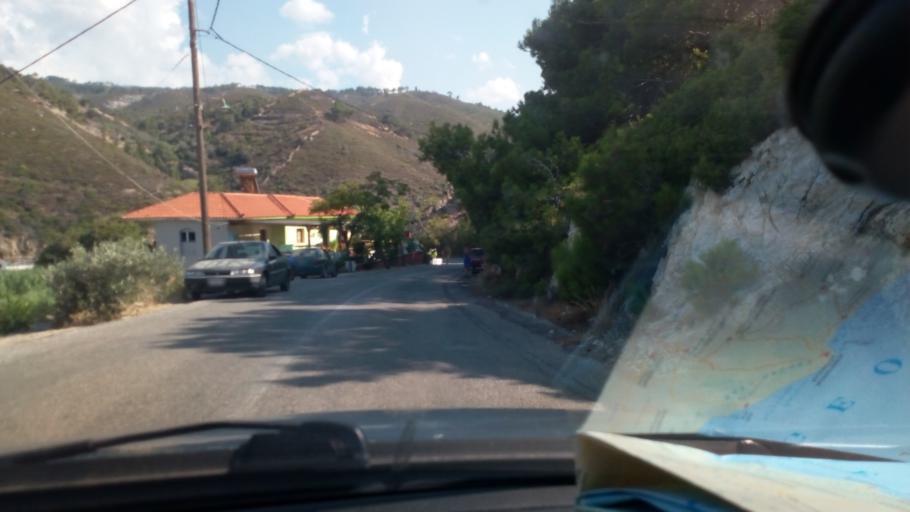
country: GR
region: North Aegean
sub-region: Nomos Samou
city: Agios Kirykos
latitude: 37.6301
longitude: 26.0890
